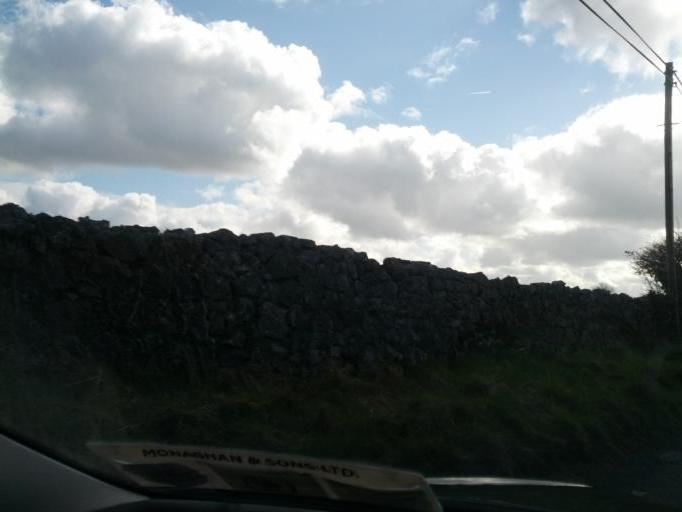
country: IE
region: Connaught
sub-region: County Galway
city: Athenry
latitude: 53.3827
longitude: -8.6943
